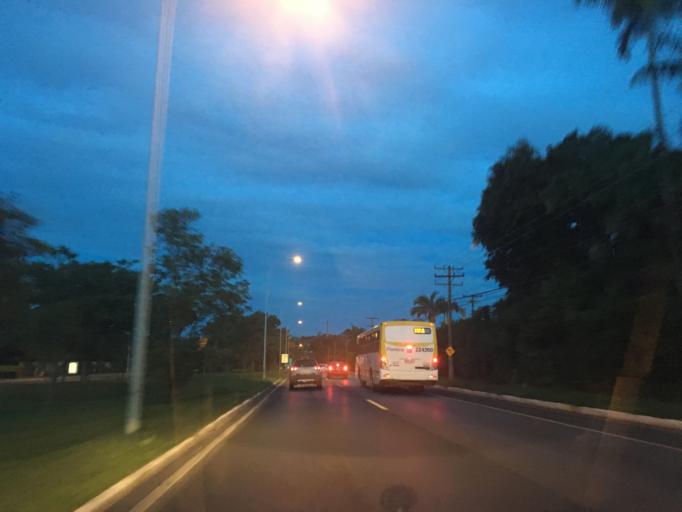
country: BR
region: Federal District
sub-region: Brasilia
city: Brasilia
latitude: -15.8571
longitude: -47.8621
